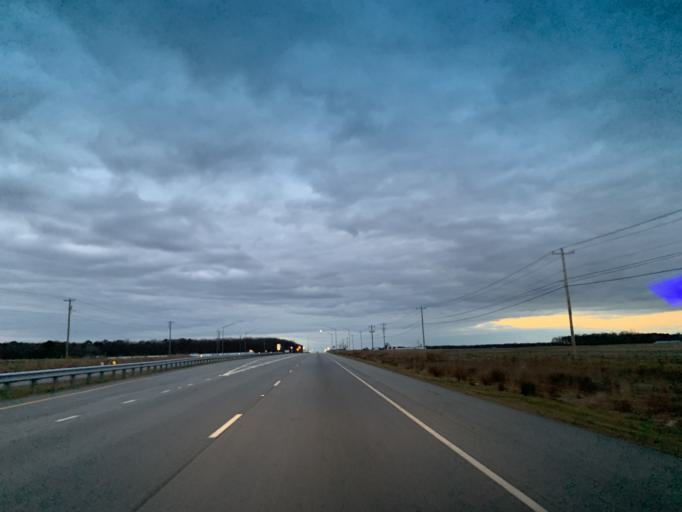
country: US
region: Maryland
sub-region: Caroline County
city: Ridgely
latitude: 38.9268
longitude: -75.9933
